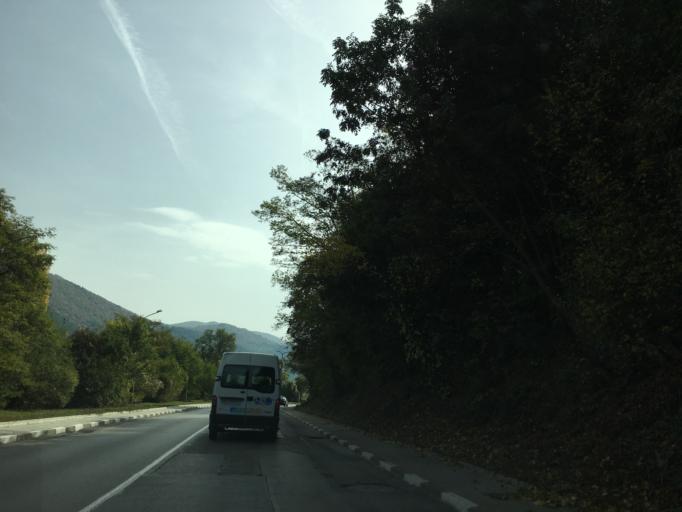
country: BG
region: Sofia-Capital
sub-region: Stolichna Obshtina
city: Sofia
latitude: 42.5933
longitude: 23.4164
